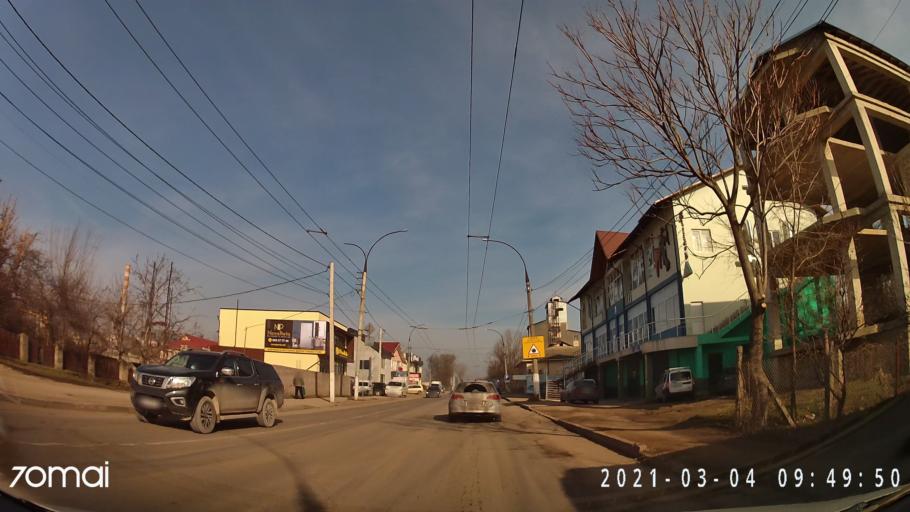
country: MD
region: Balti
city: Balti
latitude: 47.7684
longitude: 27.9308
